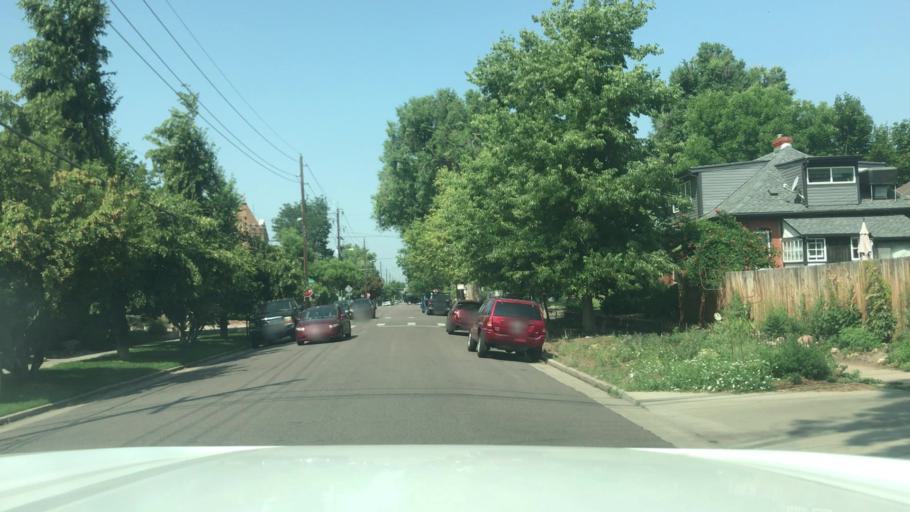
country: US
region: Colorado
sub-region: Denver County
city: Denver
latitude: 39.7021
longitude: -104.9786
